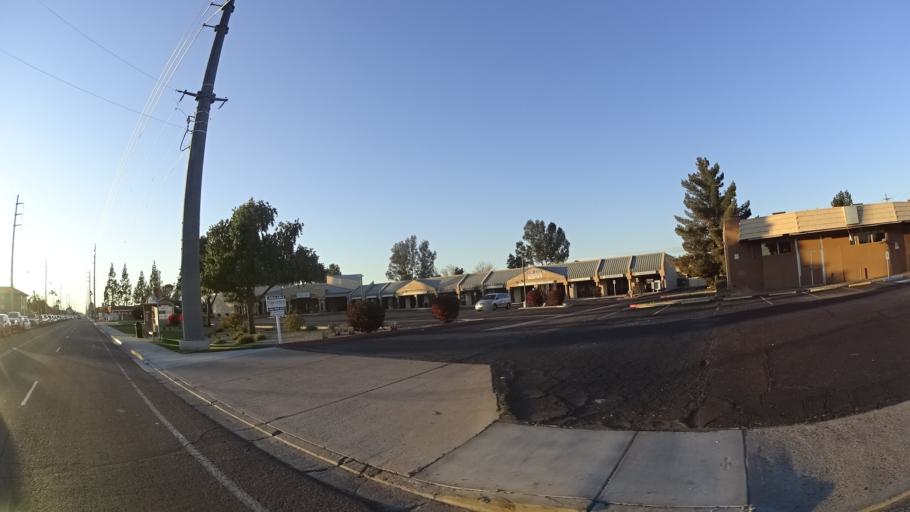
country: US
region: Arizona
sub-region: Maricopa County
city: Mesa
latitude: 33.4224
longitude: -111.8058
